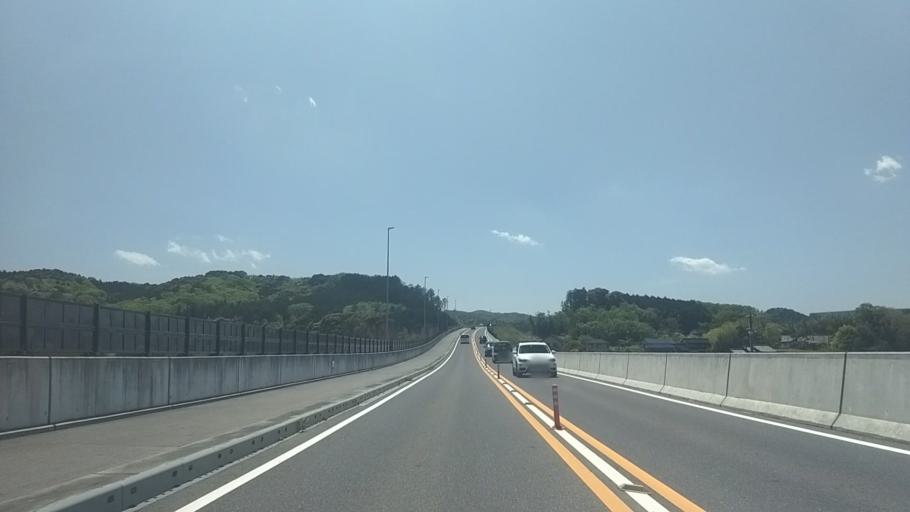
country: JP
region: Aichi
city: Gamagori
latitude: 34.9091
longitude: 137.2759
